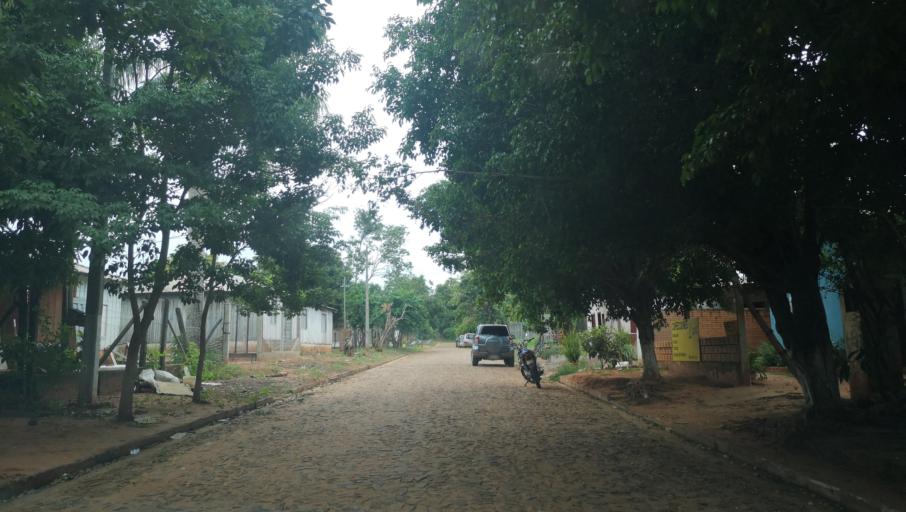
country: PY
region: San Pedro
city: Capiibary
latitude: -24.7342
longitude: -56.0198
